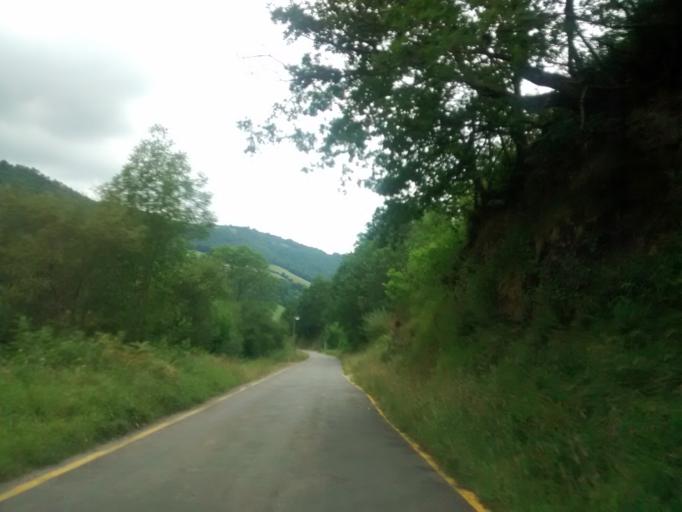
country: ES
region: Cantabria
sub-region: Provincia de Cantabria
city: Vega de Pas
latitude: 43.1418
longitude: -3.7653
